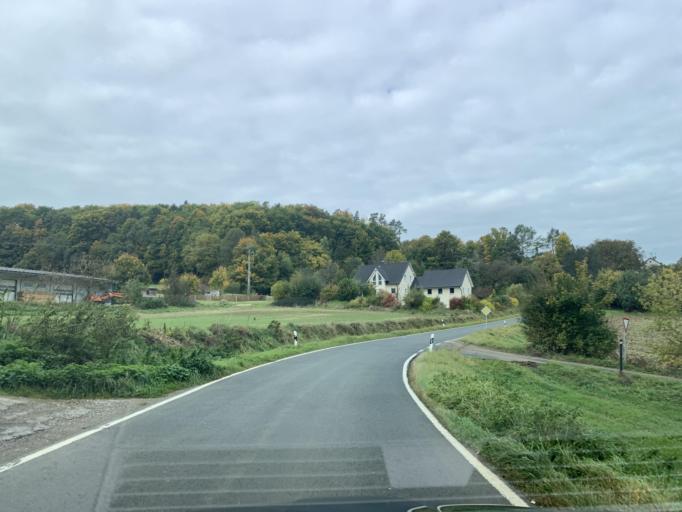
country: DE
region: Bavaria
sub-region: Upper Franconia
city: Gossweinstein
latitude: 49.7864
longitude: 11.3131
